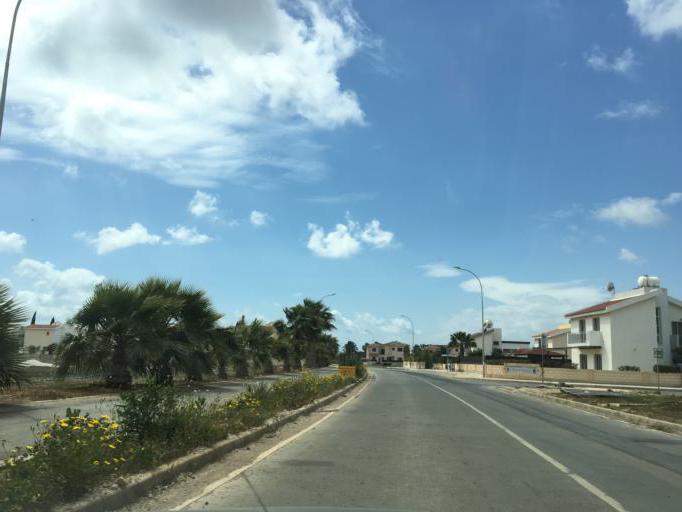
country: CY
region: Ammochostos
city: Liopetri
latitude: 34.9767
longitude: 33.9111
